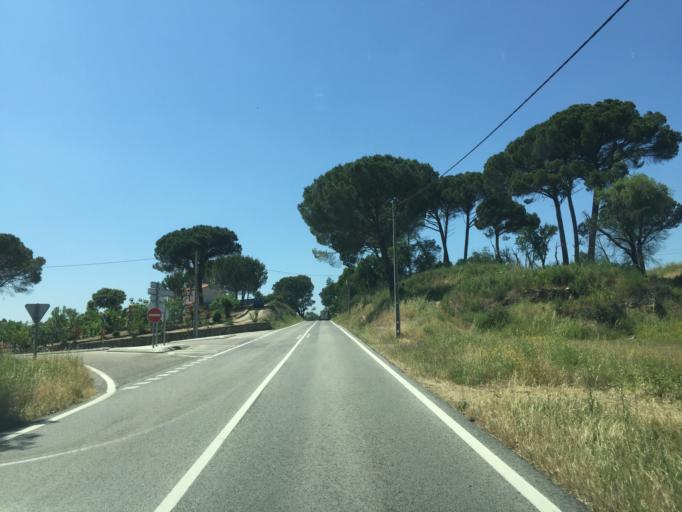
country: PT
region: Santarem
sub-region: Constancia
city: Constancia
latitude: 39.4812
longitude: -8.3212
